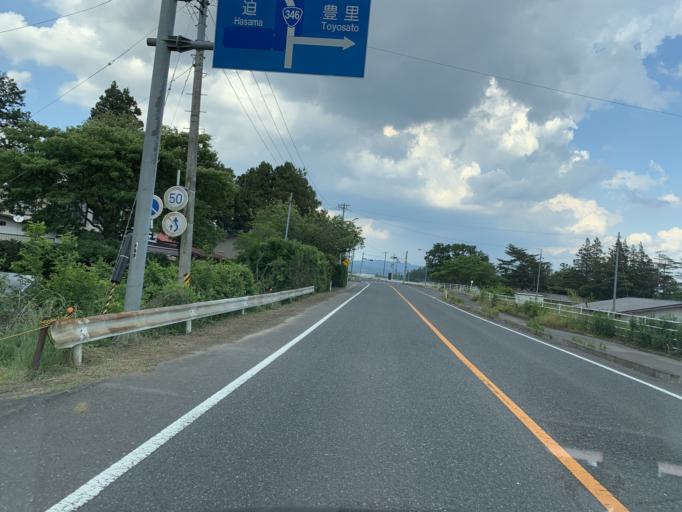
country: JP
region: Miyagi
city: Wakuya
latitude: 38.6474
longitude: 141.2156
